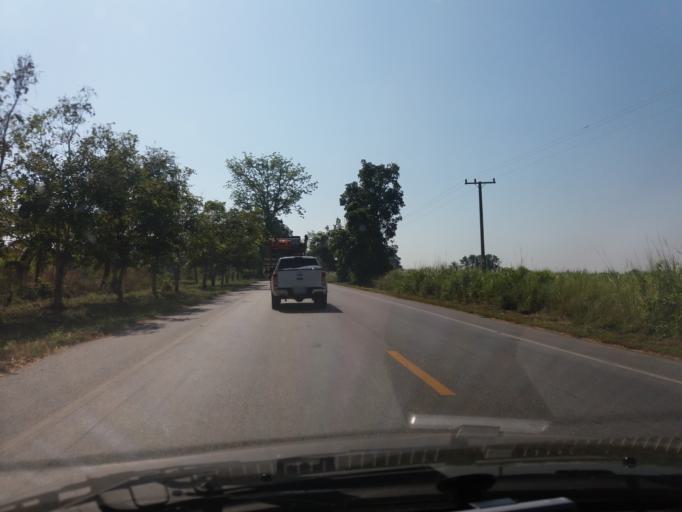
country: TH
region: Kamphaeng Phet
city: Khanu Woralaksaburi
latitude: 16.1436
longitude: 99.8127
